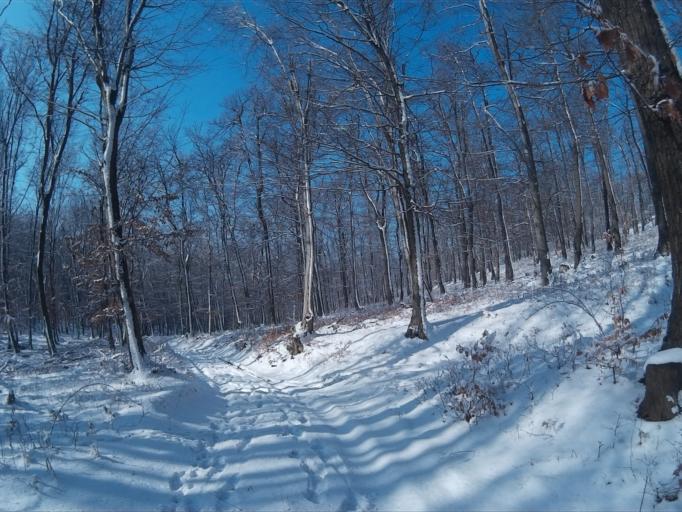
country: HU
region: Komarom-Esztergom
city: Labatlan
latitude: 47.7060
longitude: 18.5092
